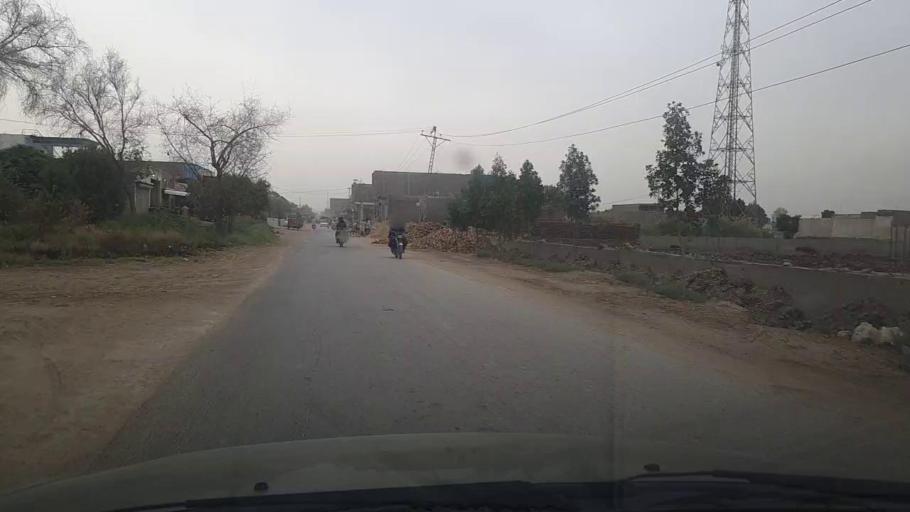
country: PK
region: Sindh
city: Daur
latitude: 26.4573
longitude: 68.3037
